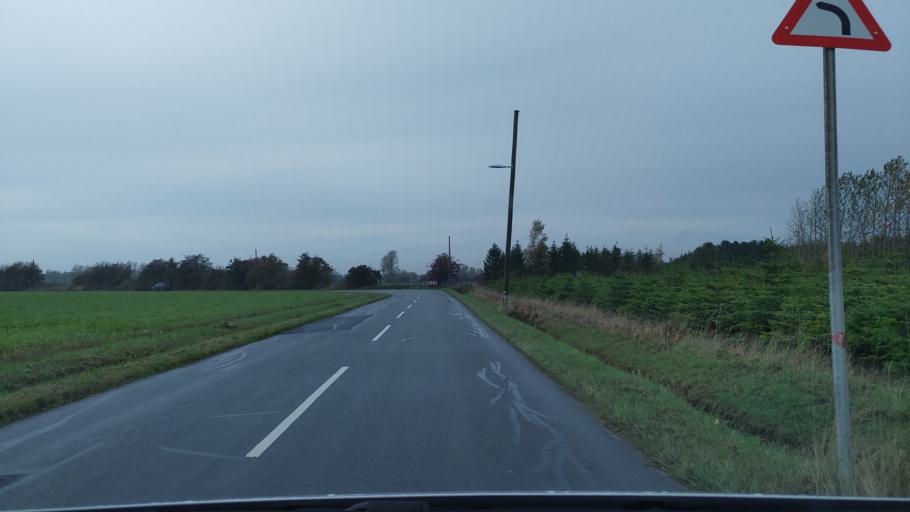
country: DK
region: Capital Region
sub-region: Tarnby Kommune
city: Tarnby
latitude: 55.5750
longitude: 12.6130
